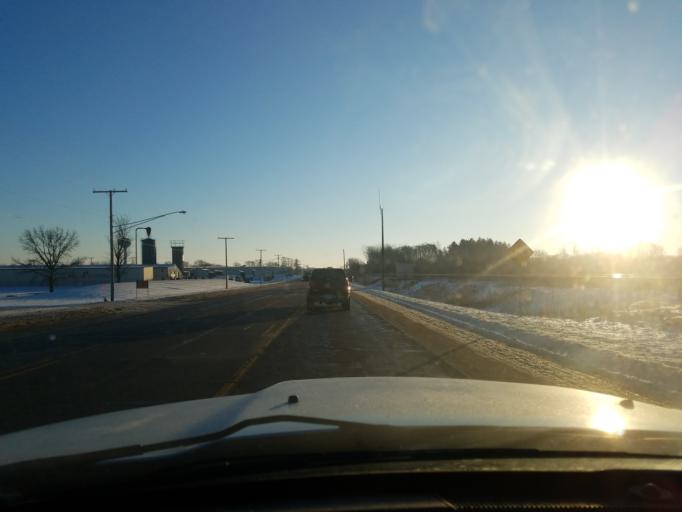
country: US
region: Indiana
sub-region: Elkhart County
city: Nappanee
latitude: 41.4432
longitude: -86.0297
